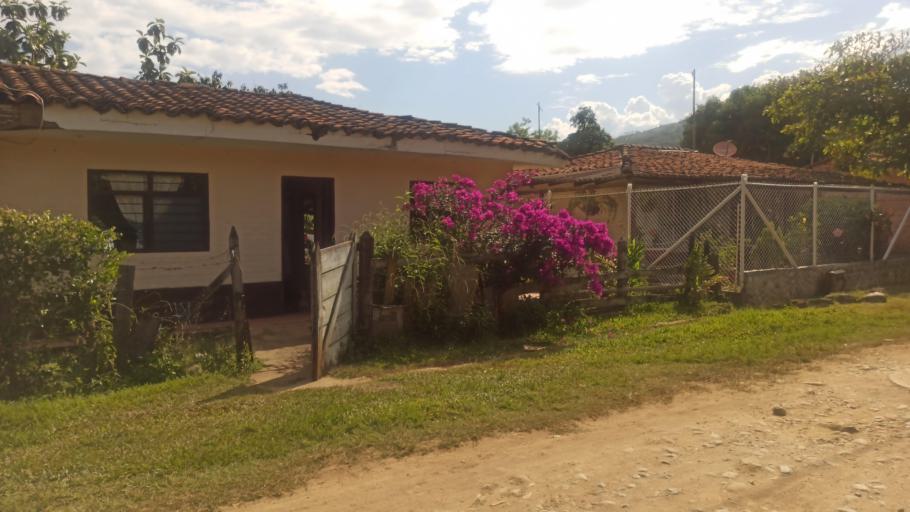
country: CO
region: Valle del Cauca
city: Jamundi
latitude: 3.1716
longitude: -76.5938
